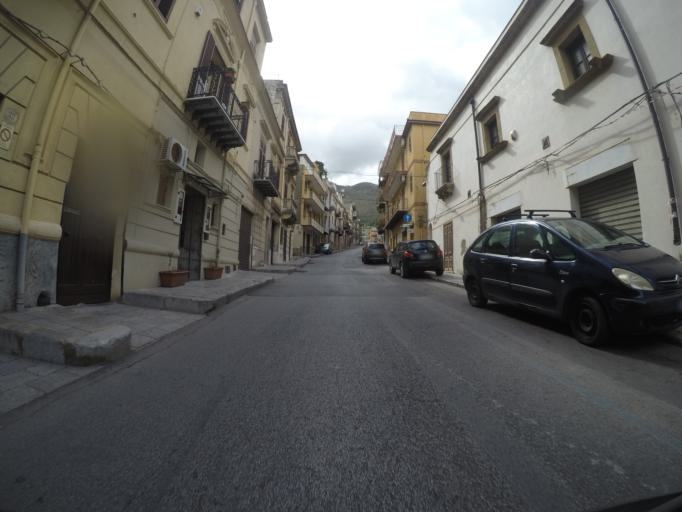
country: IT
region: Sicily
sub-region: Palermo
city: Carini
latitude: 38.1303
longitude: 13.1817
